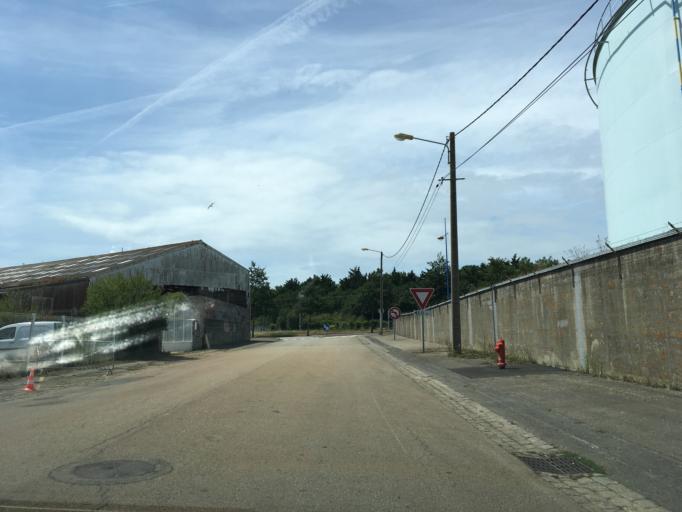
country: FR
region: Brittany
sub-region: Departement du Morbihan
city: Lorient
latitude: 47.7394
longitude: -3.3597
